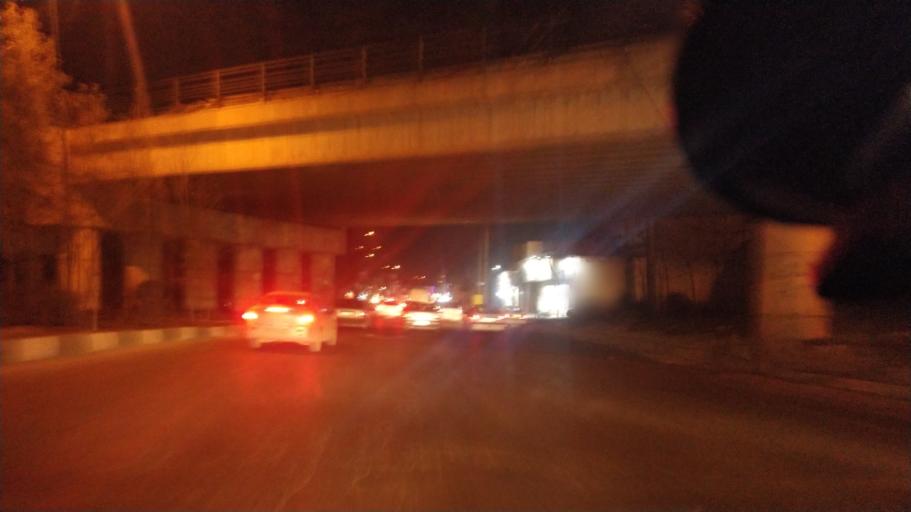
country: IR
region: Alborz
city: Karaj
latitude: 35.7860
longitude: 51.0058
